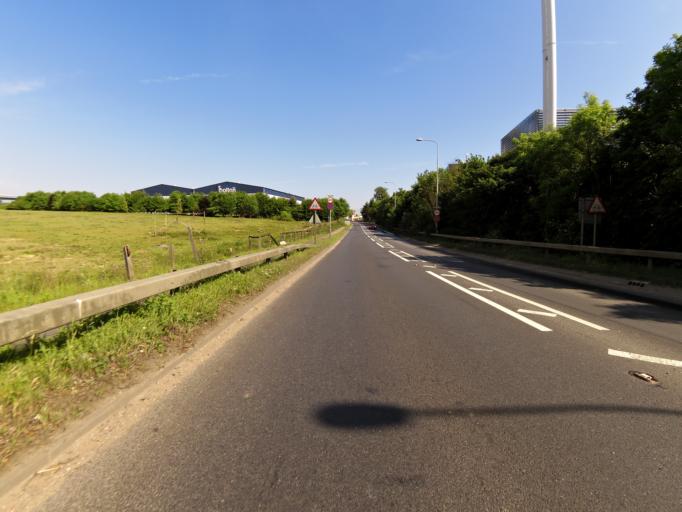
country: GB
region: England
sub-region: Suffolk
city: Bramford
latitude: 52.1031
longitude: 1.0977
